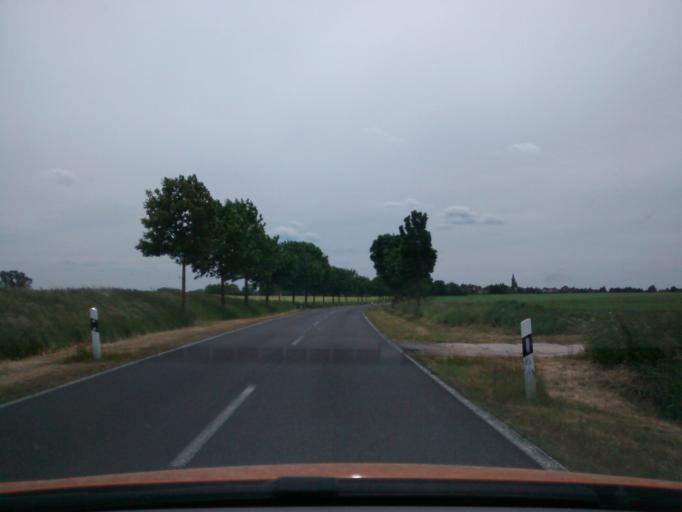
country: DE
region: Brandenburg
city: Juterbog
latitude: 51.9570
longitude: 13.0852
